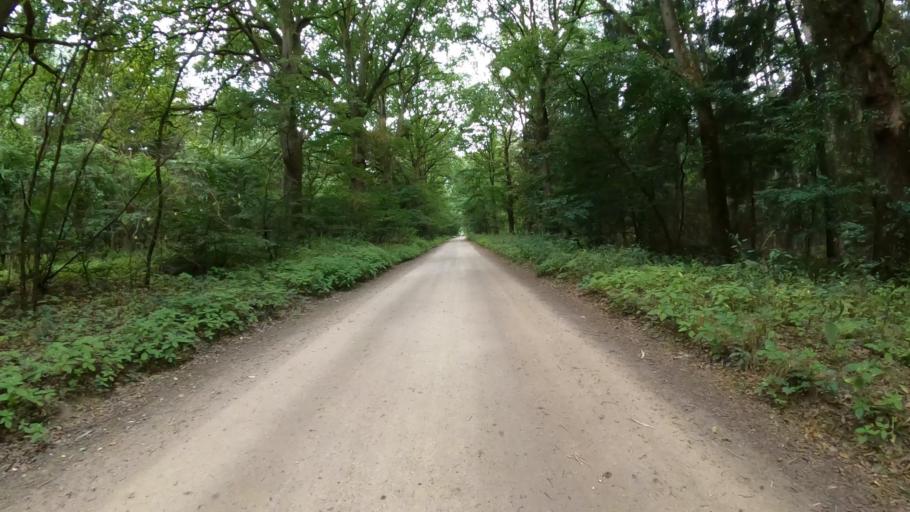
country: DE
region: Lower Saxony
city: Kakenstorf
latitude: 53.3187
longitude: 9.7422
